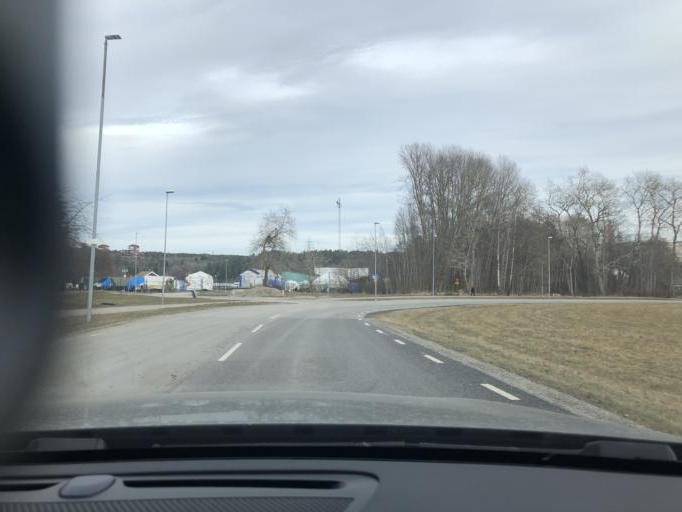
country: SE
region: Stockholm
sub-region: Botkyrka Kommun
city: Fittja
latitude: 59.2395
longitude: 17.8624
